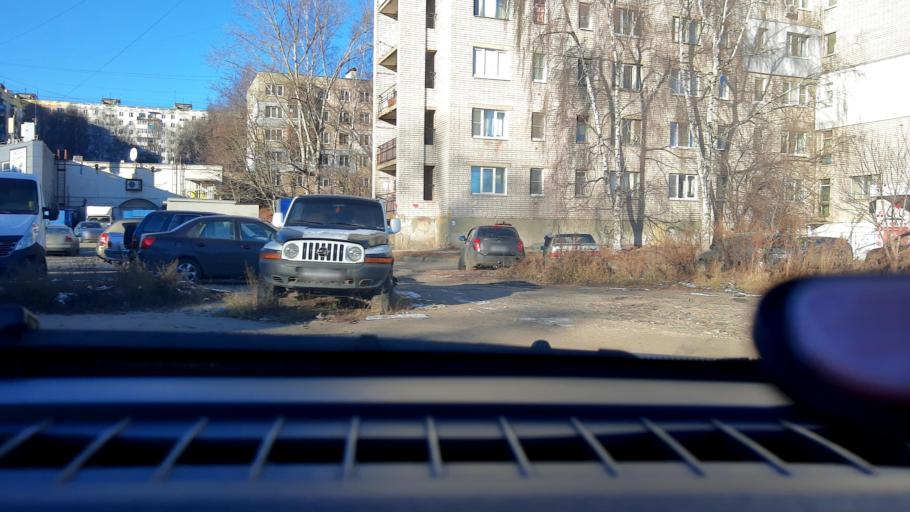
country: RU
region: Nizjnij Novgorod
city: Nizhniy Novgorod
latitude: 56.2284
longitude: 43.9497
